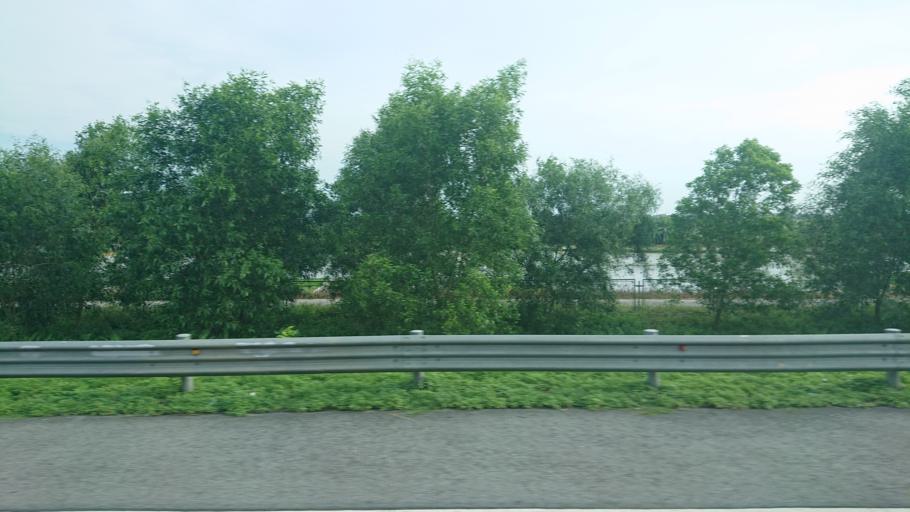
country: VN
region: Hai Phong
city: An Lao
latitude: 20.7990
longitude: 106.5370
